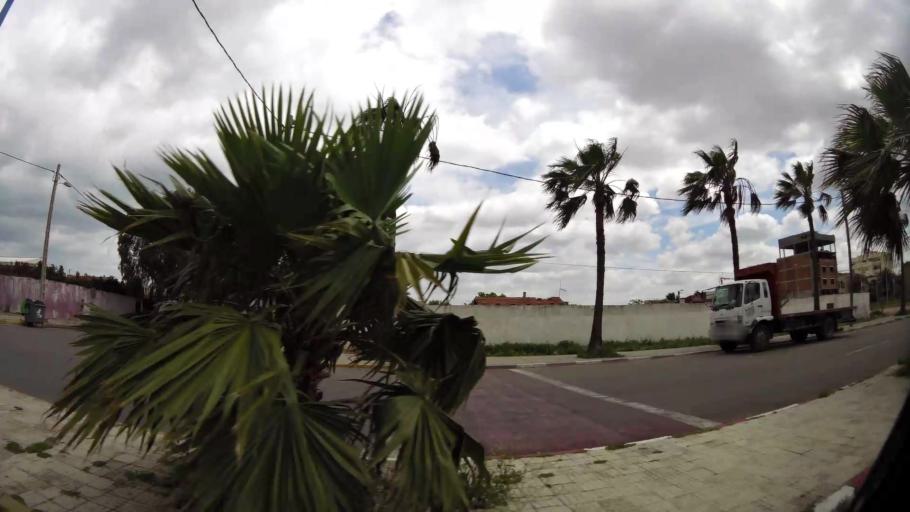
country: MA
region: Grand Casablanca
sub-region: Casablanca
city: Casablanca
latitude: 33.6127
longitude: -7.5506
